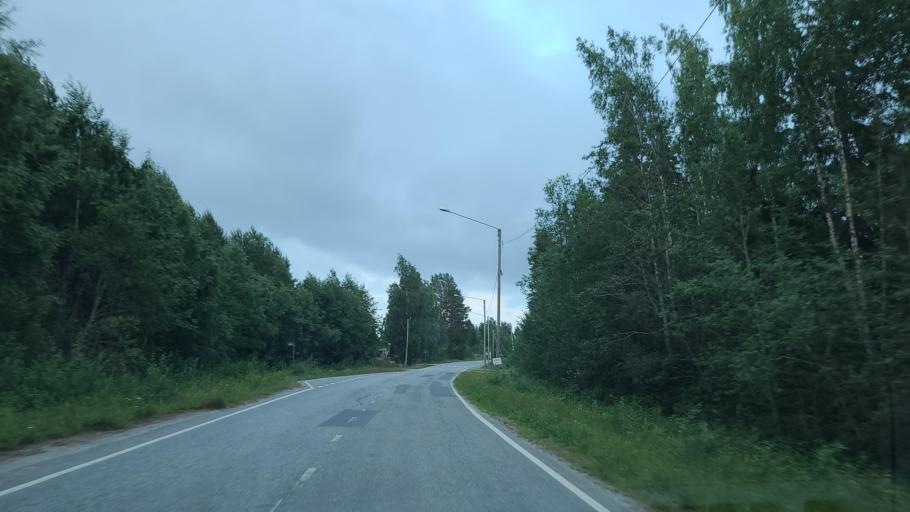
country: FI
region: Ostrobothnia
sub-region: Vaasa
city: Replot
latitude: 63.2854
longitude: 21.1200
